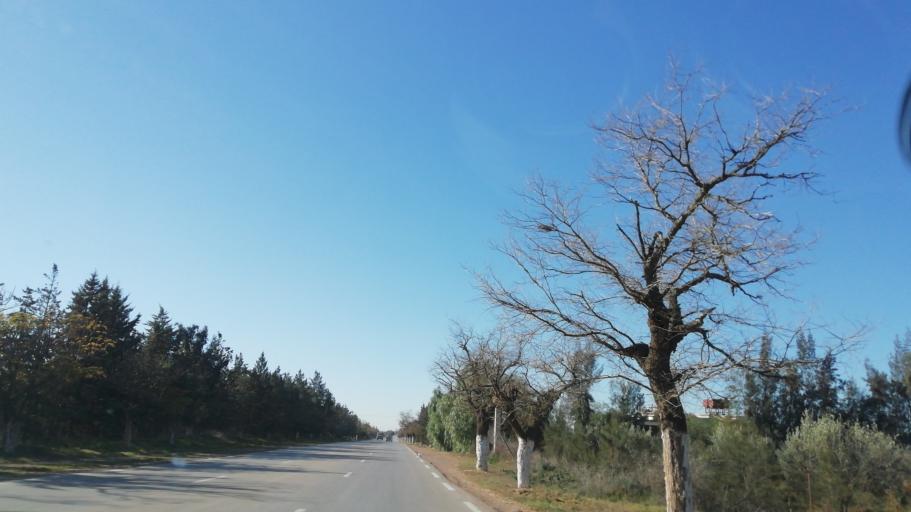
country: MA
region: Oriental
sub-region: Oujda-Angad
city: Oujda
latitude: 34.8141
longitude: -1.8097
